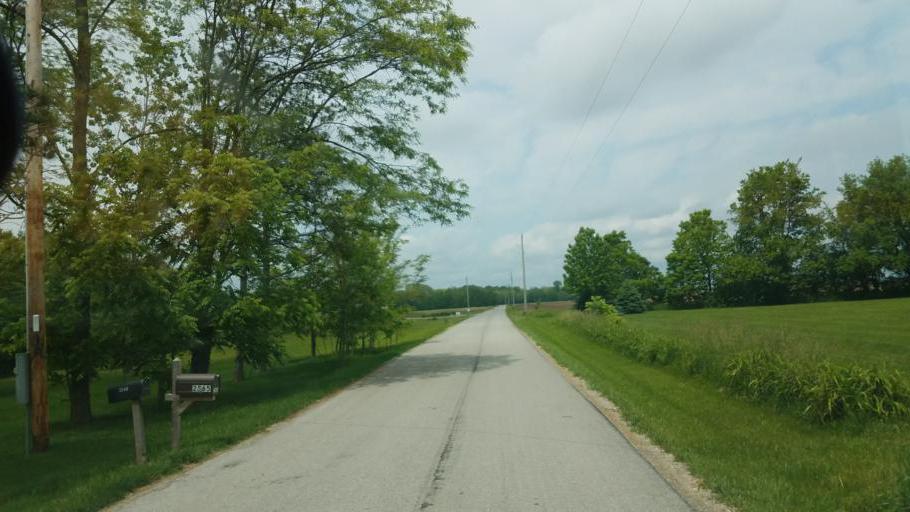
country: US
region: Ohio
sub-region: Marion County
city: Prospect
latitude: 40.3611
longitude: -83.1819
